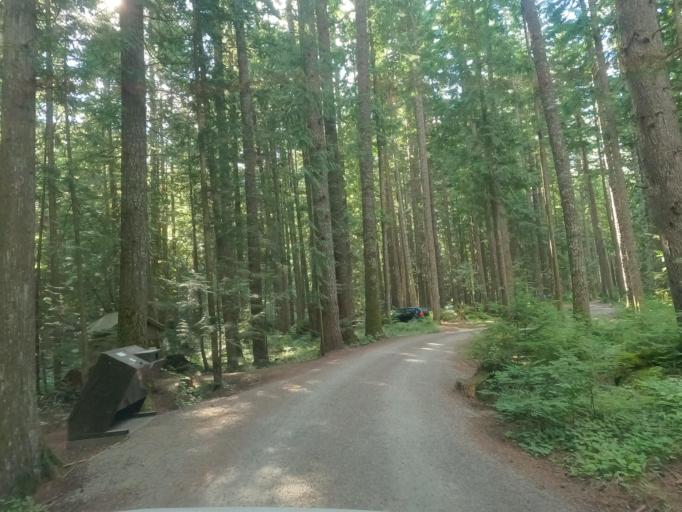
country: CA
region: British Columbia
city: Whistler
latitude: 50.0643
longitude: -123.1001
